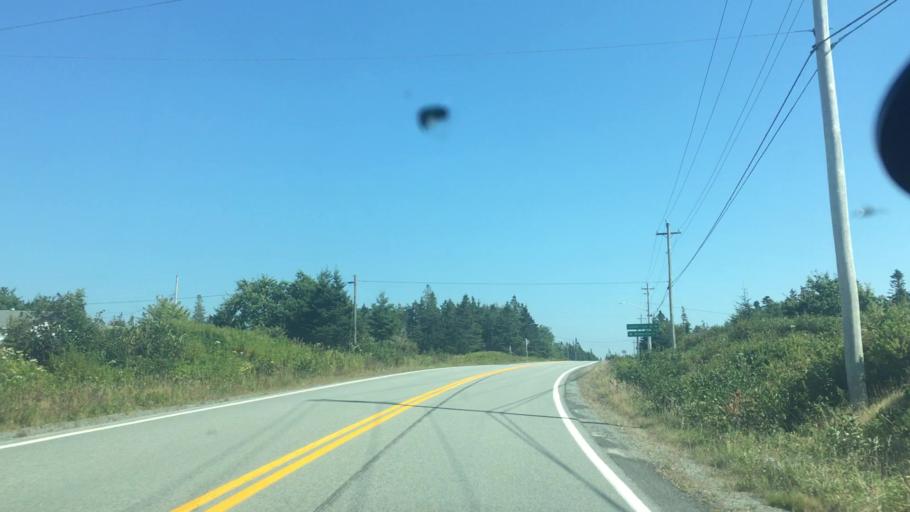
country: CA
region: Nova Scotia
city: New Glasgow
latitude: 44.9206
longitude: -62.3040
